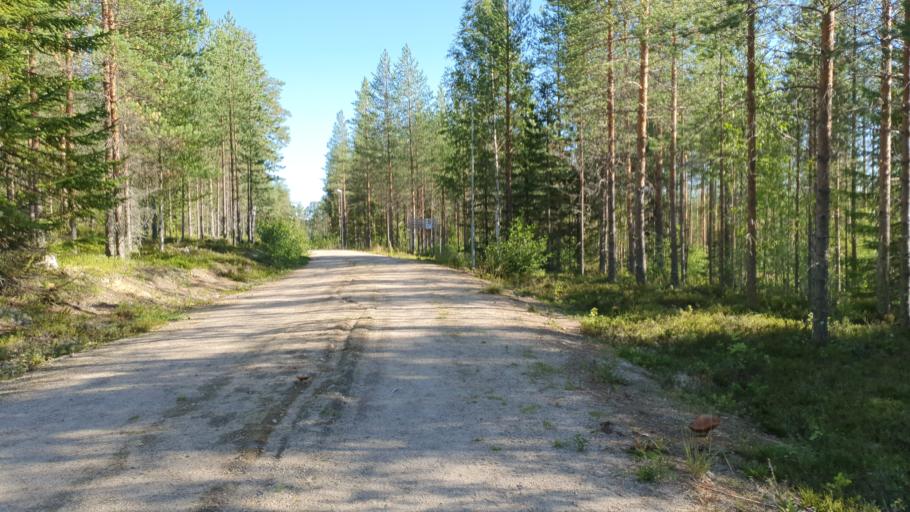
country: FI
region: Kainuu
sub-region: Kehys-Kainuu
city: Kuhmo
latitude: 64.1096
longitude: 29.5040
